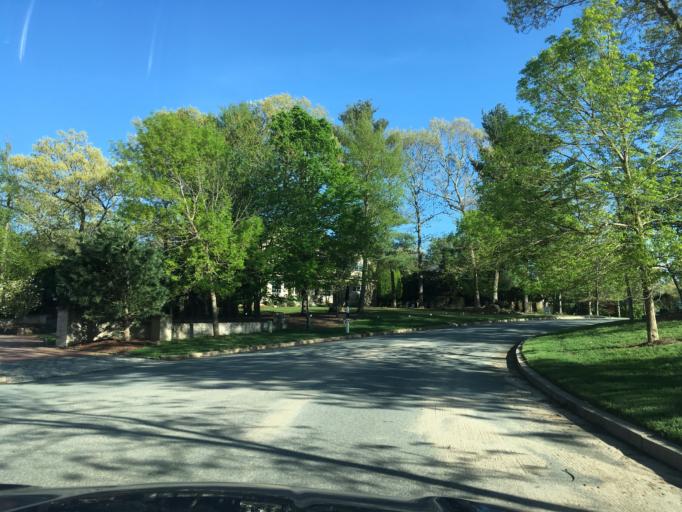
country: US
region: Rhode Island
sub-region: Washington County
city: Exeter
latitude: 41.6129
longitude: -71.5260
